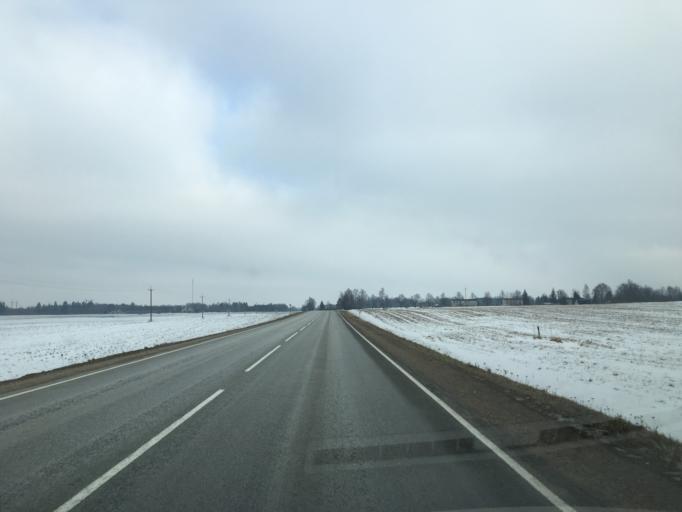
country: EE
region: Tartu
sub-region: Elva linn
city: Elva
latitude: 58.1194
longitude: 26.2403
